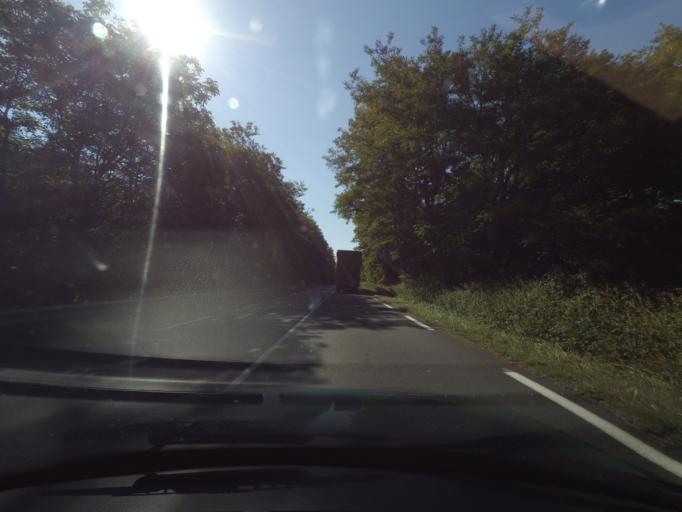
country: FR
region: Poitou-Charentes
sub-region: Departement de la Vienne
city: Lussac-les-Chateaux
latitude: 46.4139
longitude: 0.6853
